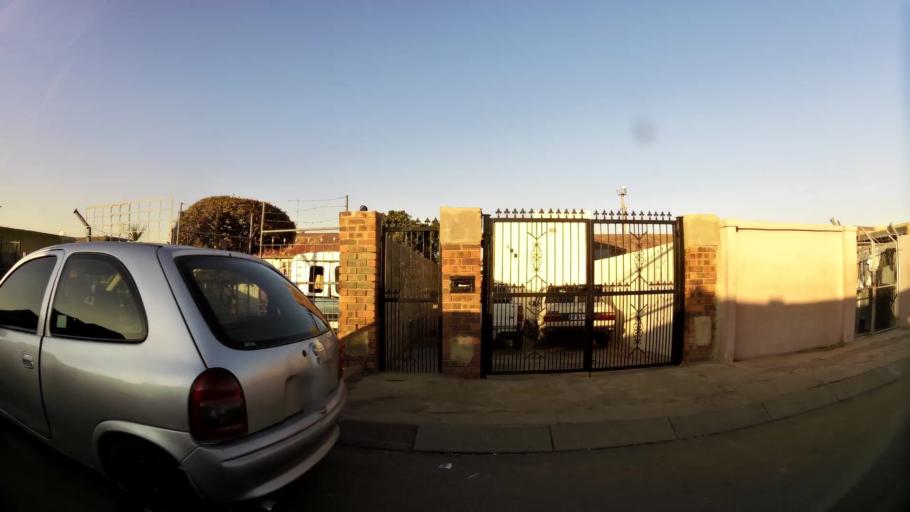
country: ZA
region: Gauteng
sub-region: City of Johannesburg Metropolitan Municipality
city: Soweto
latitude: -26.2514
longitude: 27.8812
